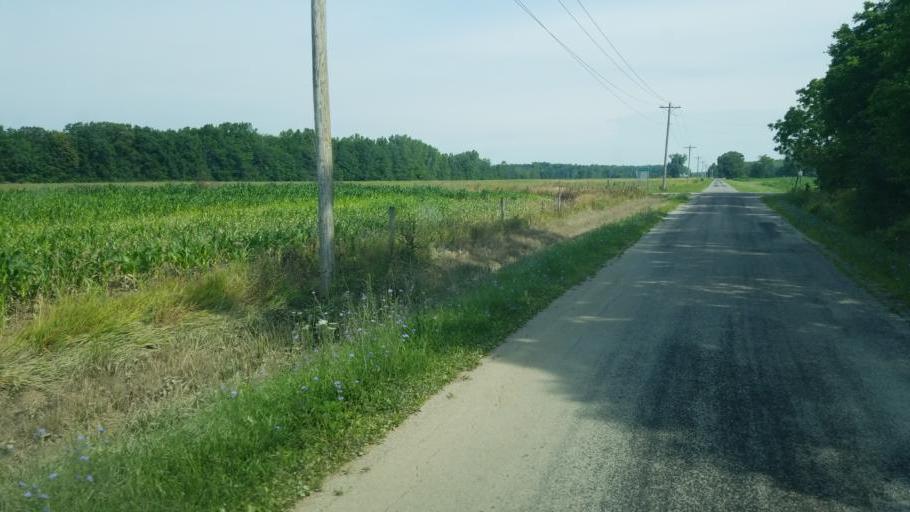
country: US
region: Ohio
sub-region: Wyandot County
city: Upper Sandusky
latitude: 40.6866
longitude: -83.3429
